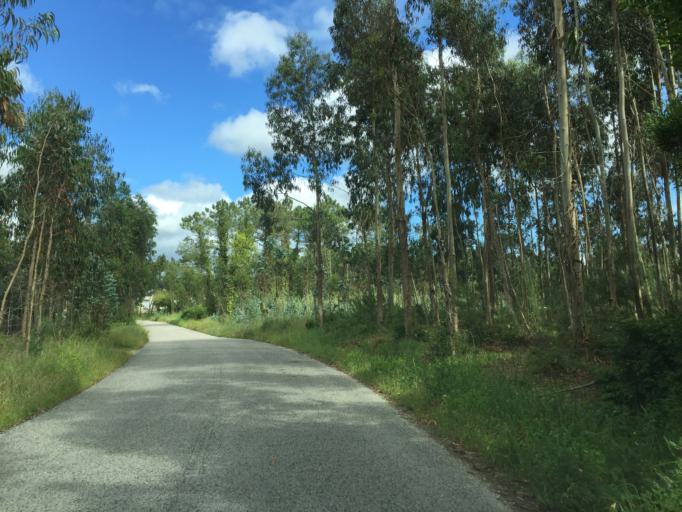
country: PT
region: Coimbra
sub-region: Figueira da Foz
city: Tavarede
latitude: 40.2101
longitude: -8.8308
